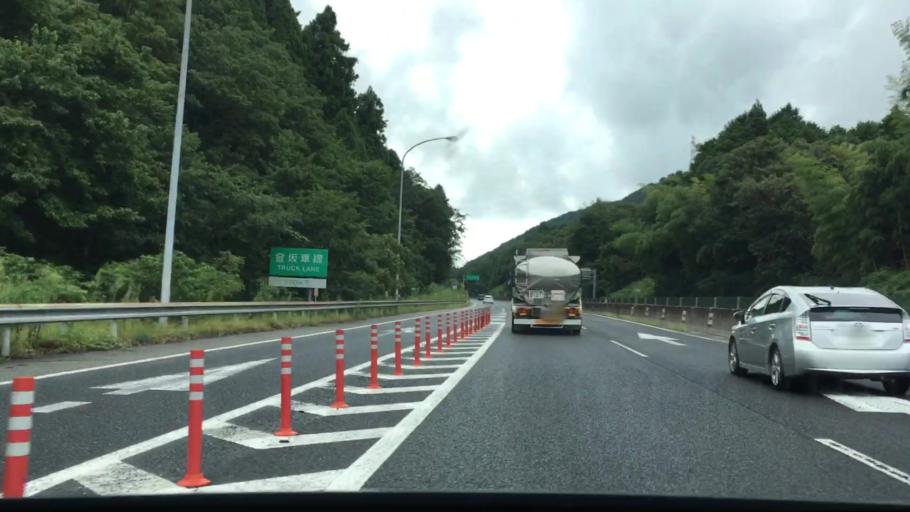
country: JP
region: Hyogo
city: Yamazakicho-nakabirose
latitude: 35.0329
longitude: 134.4839
